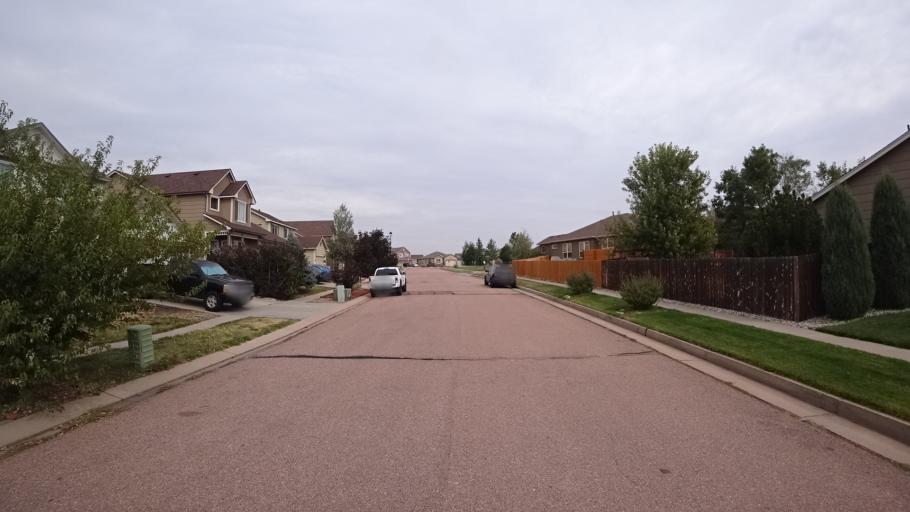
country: US
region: Colorado
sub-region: El Paso County
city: Cimarron Hills
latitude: 38.9163
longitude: -104.6917
